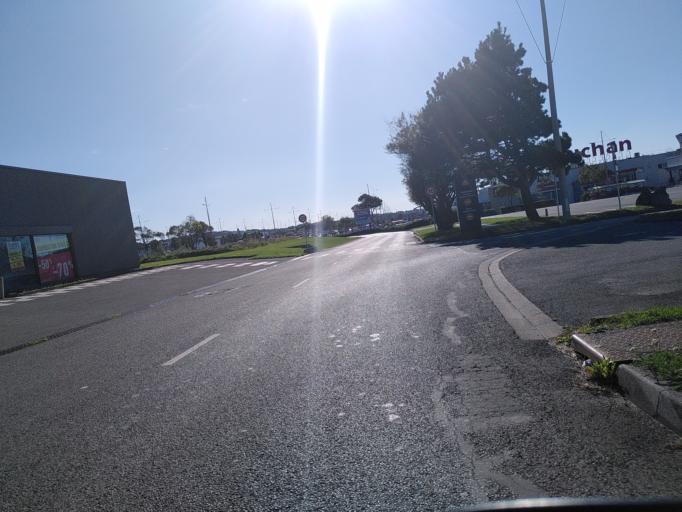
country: FR
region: Nord-Pas-de-Calais
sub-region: Departement du Pas-de-Calais
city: La Capelle-les-Boulogne
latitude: 50.7353
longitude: 1.6783
